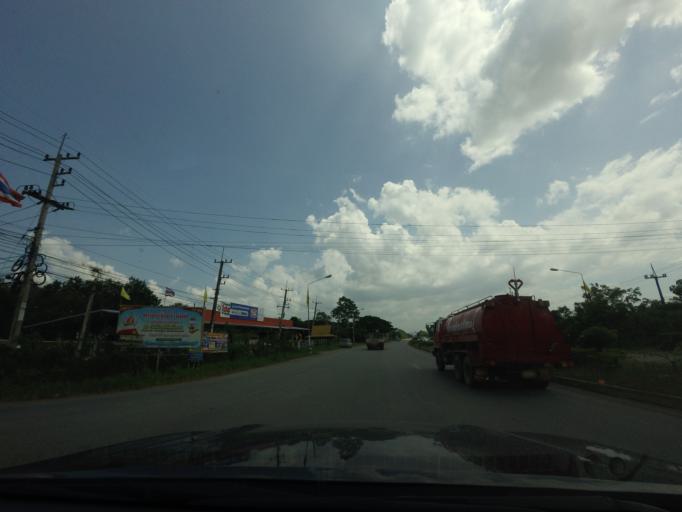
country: TH
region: Phetchabun
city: Phetchabun
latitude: 16.2485
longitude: 101.0706
